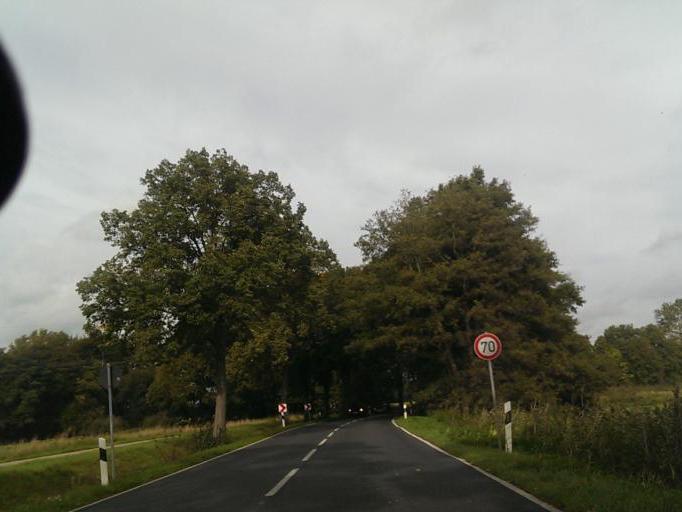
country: DE
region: Lower Saxony
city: Wunstorf
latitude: 52.4557
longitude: 9.4661
